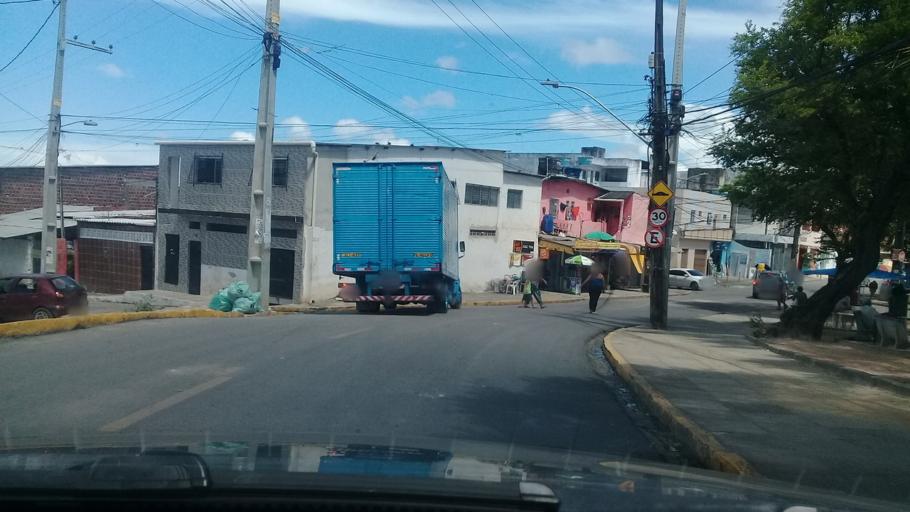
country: BR
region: Pernambuco
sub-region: Jaboatao Dos Guararapes
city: Jaboatao dos Guararapes
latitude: -8.1208
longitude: -34.9458
